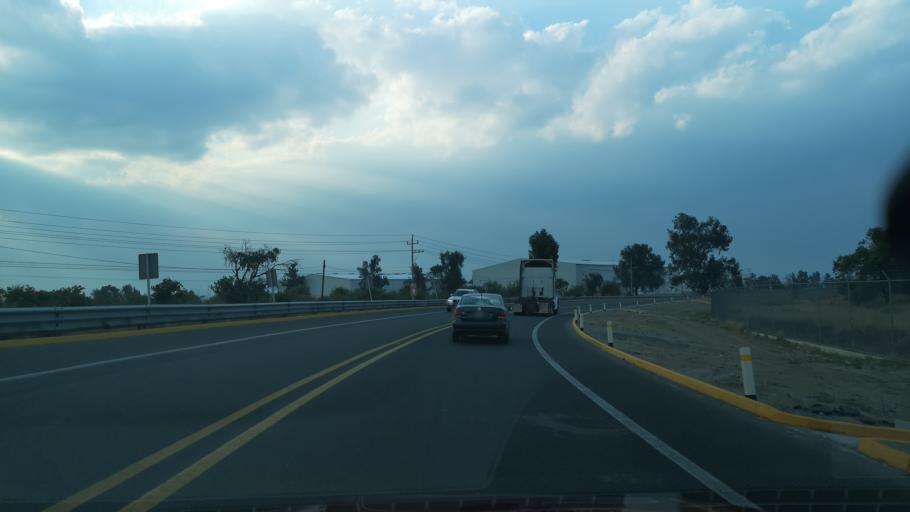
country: MX
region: Puebla
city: Huejotzingo
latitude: 19.1533
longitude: -98.3767
